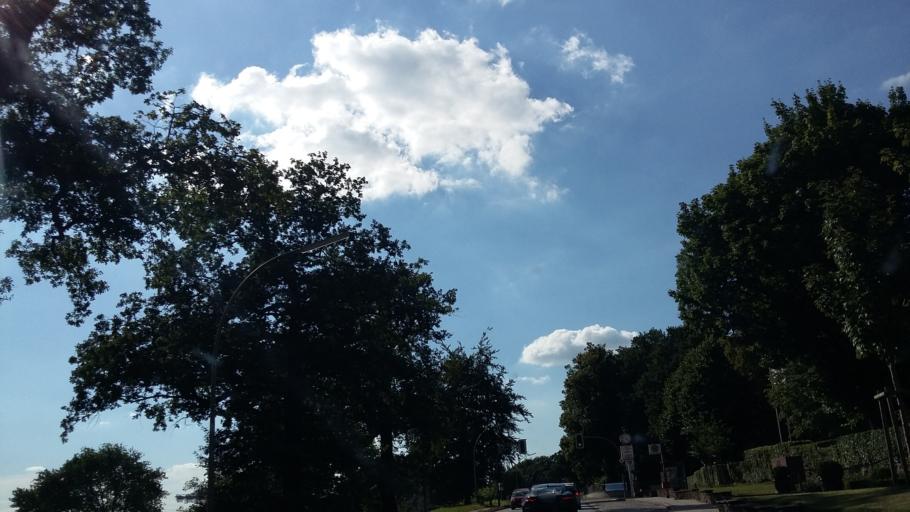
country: DE
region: Hamburg
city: Eidelstedt
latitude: 53.5492
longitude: 9.8530
